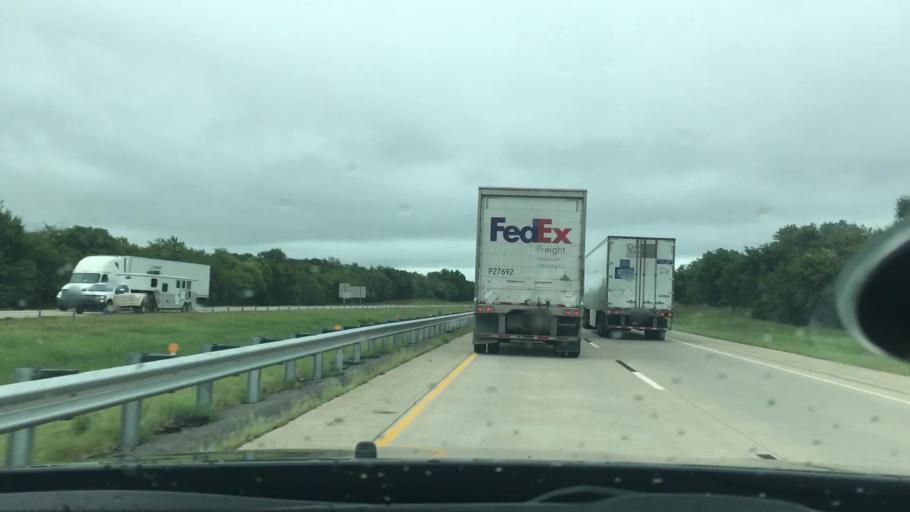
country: US
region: Oklahoma
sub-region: McIntosh County
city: Checotah
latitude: 35.4591
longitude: -95.6252
